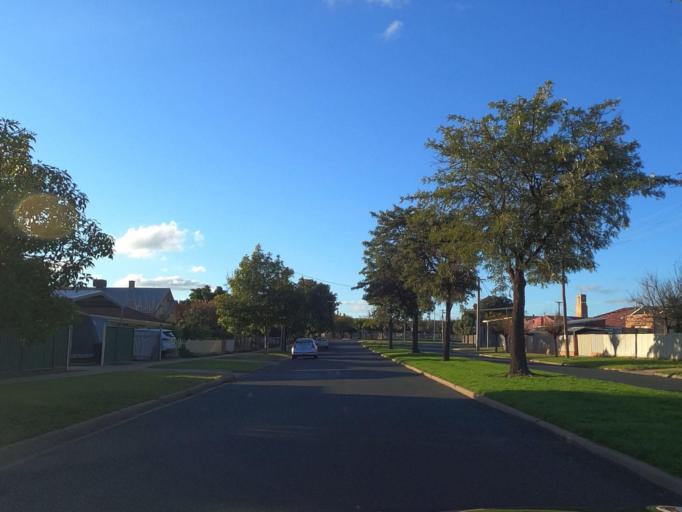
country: AU
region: Victoria
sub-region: Swan Hill
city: Swan Hill
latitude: -35.3452
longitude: 143.5559
